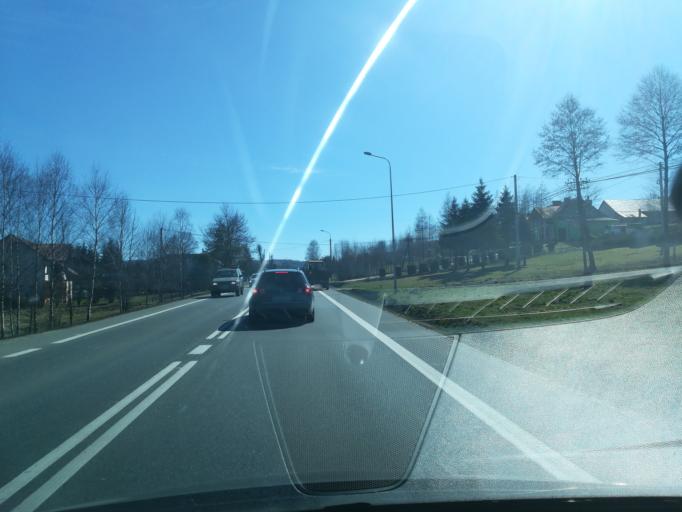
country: PL
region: Subcarpathian Voivodeship
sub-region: Powiat strzyzowski
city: Polomia
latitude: 49.8927
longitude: 21.8924
